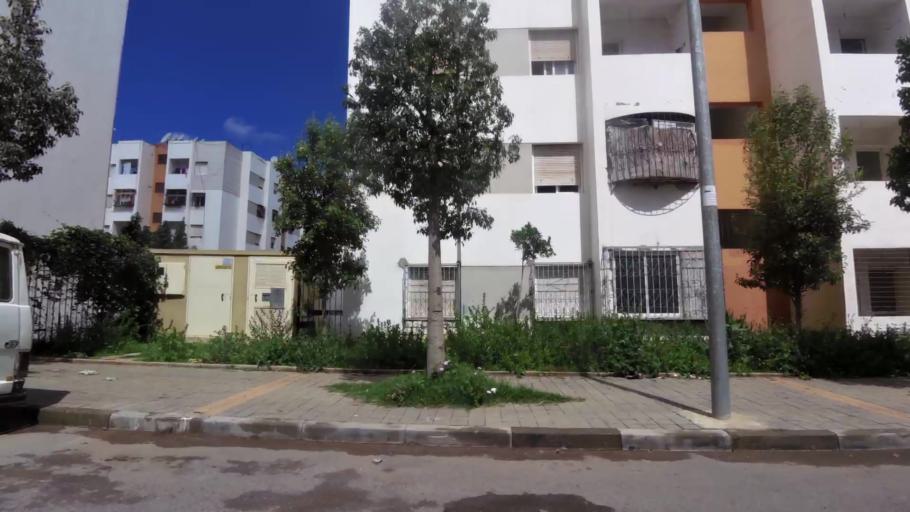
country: MA
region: Grand Casablanca
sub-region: Nouaceur
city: Dar Bouazza
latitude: 33.5359
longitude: -7.7168
